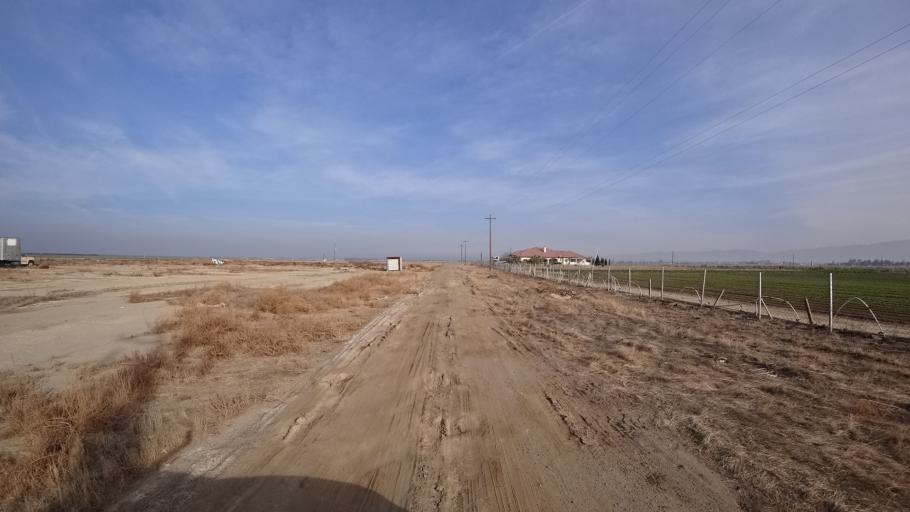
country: US
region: California
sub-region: Kern County
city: Lamont
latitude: 35.3234
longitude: -118.9484
